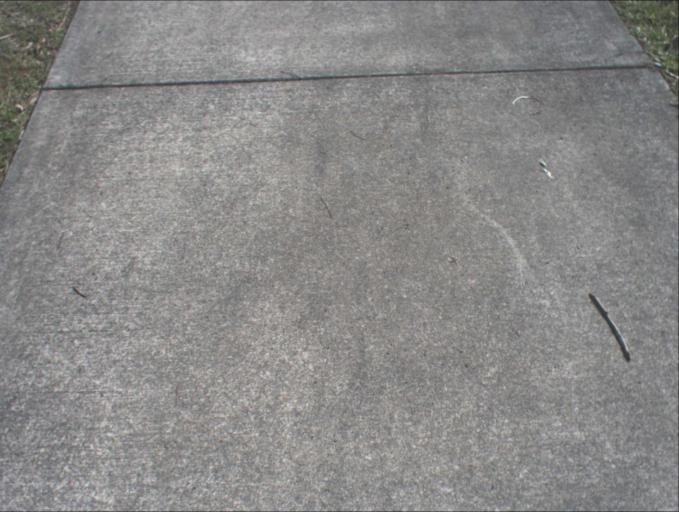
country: AU
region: Queensland
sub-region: Logan
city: Windaroo
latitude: -27.7218
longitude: 153.1737
